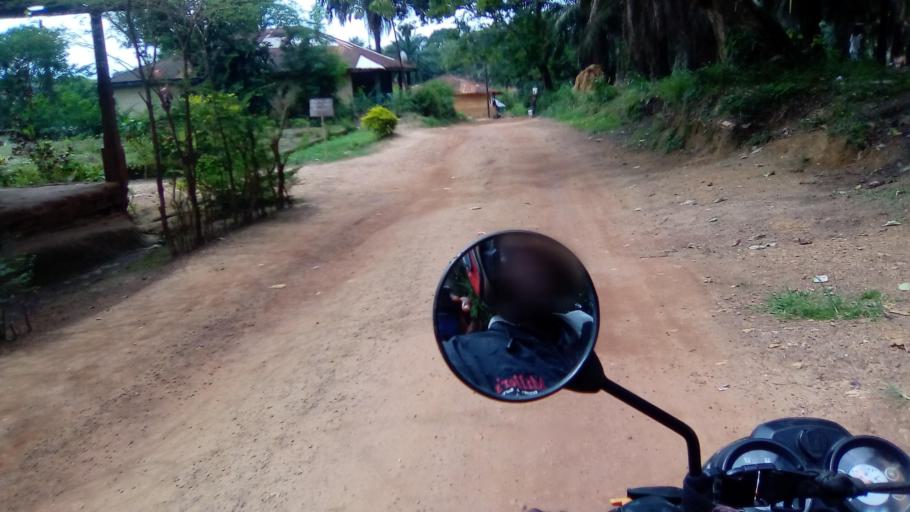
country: SL
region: Southern Province
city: Bo
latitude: 7.9607
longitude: -11.7275
